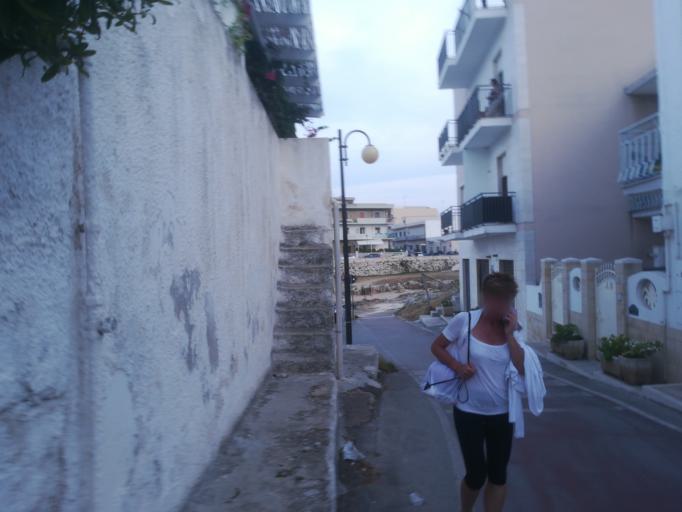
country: IT
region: Apulia
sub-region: Provincia di Bari
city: Monopoli
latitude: 40.9483
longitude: 17.3062
